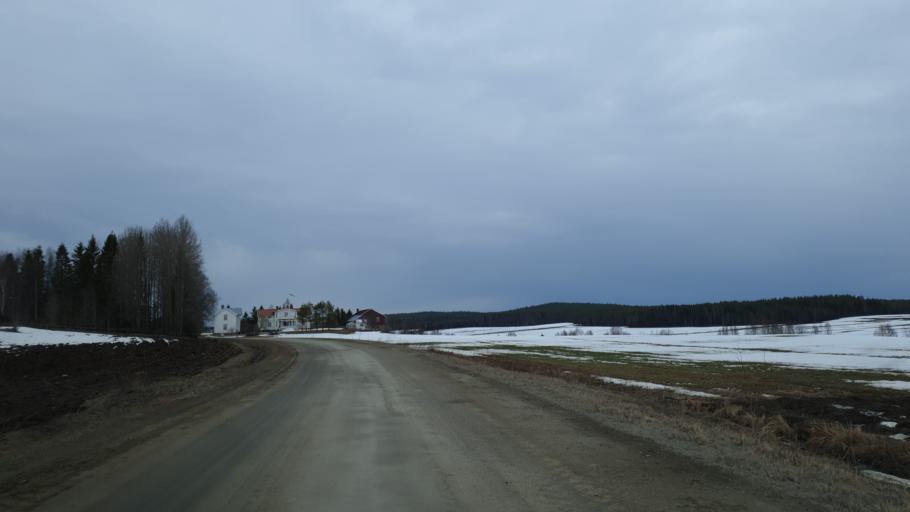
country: SE
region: Vaesterbotten
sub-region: Skelleftea Kommun
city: Burea
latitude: 64.3325
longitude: 21.1340
